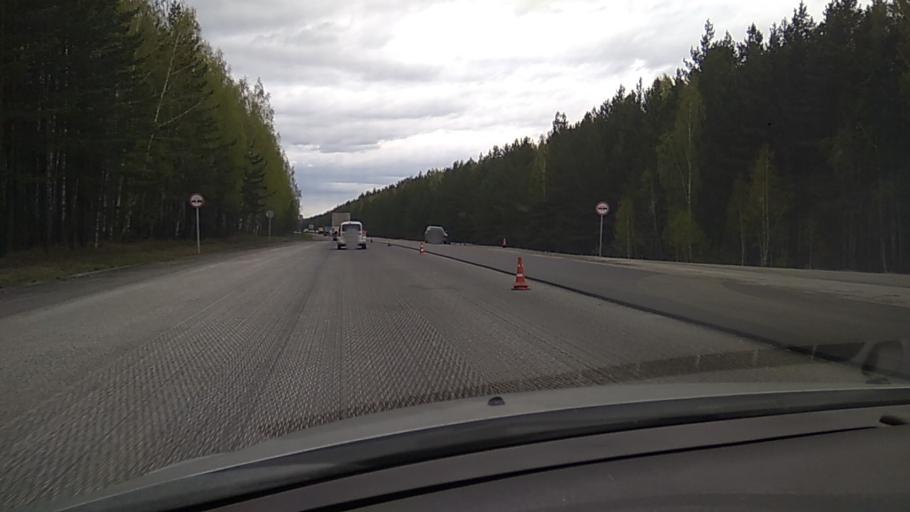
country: RU
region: Sverdlovsk
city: Verkhneye Dubrovo
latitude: 56.6912
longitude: 61.1049
